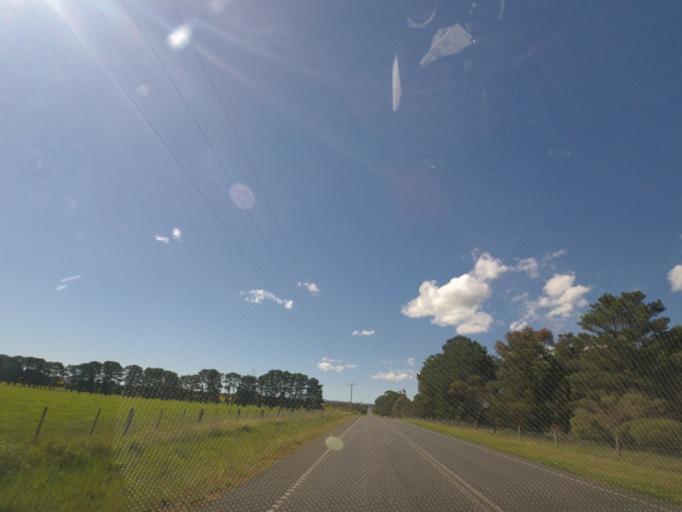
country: AU
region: Victoria
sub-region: Moorabool
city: Bacchus Marsh
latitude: -37.6736
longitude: 144.2280
